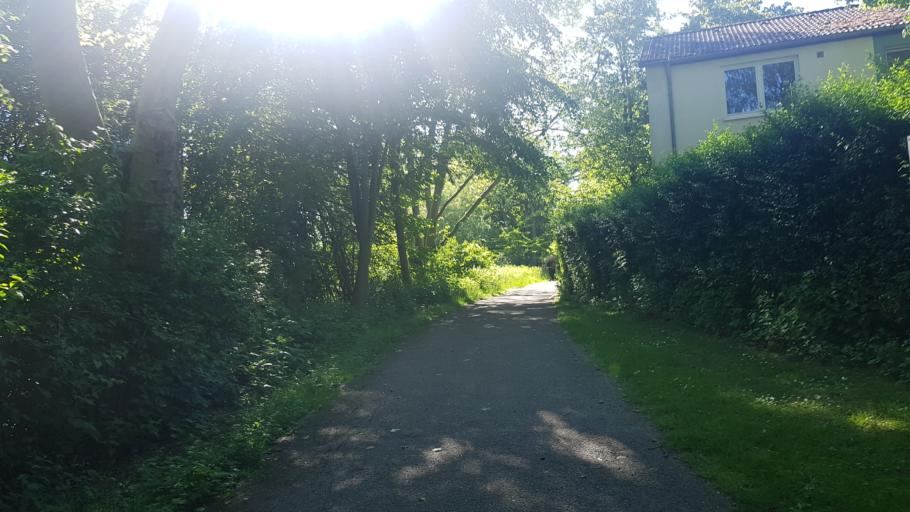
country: DE
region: North Rhine-Westphalia
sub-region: Regierungsbezirk Dusseldorf
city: Essen
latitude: 51.4679
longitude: 7.0515
